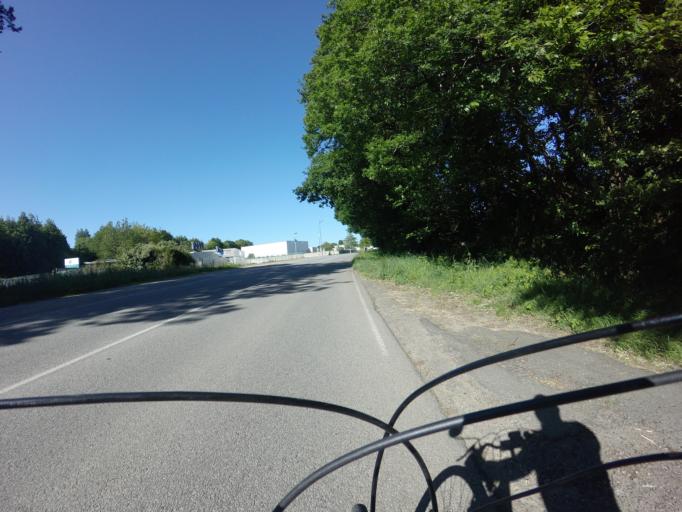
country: FR
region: Brittany
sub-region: Departement du Finistere
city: Plomelin
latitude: 47.9690
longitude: -4.1438
